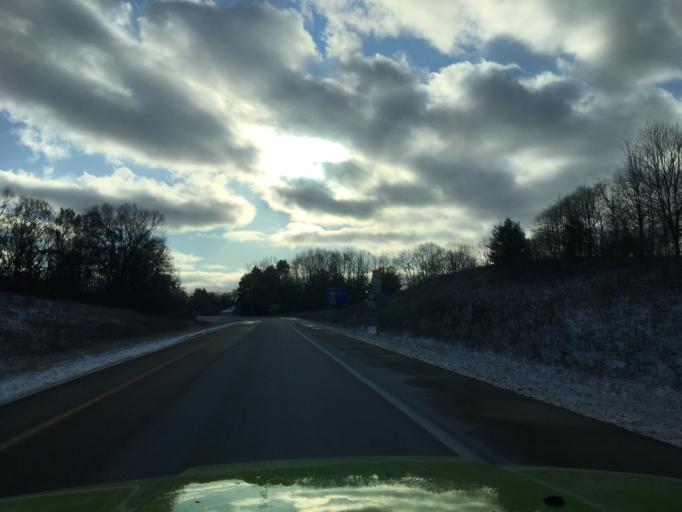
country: US
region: Michigan
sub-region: Kent County
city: Cedar Springs
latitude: 43.1779
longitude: -85.5773
